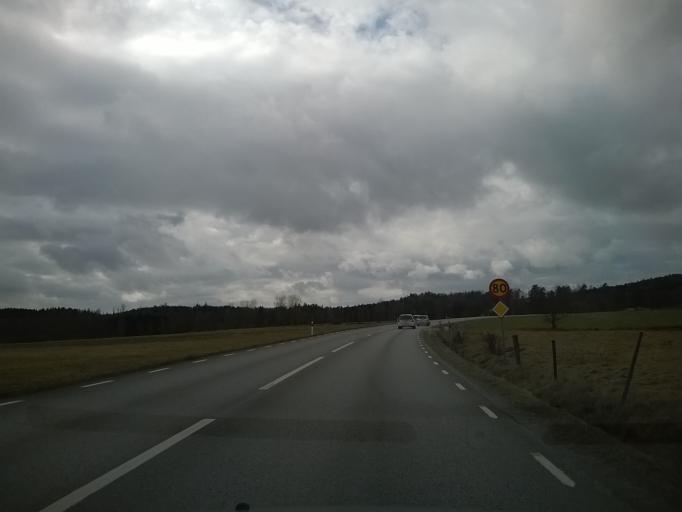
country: SE
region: Halland
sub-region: Varbergs Kommun
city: Tvaaker
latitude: 57.1430
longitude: 12.5150
